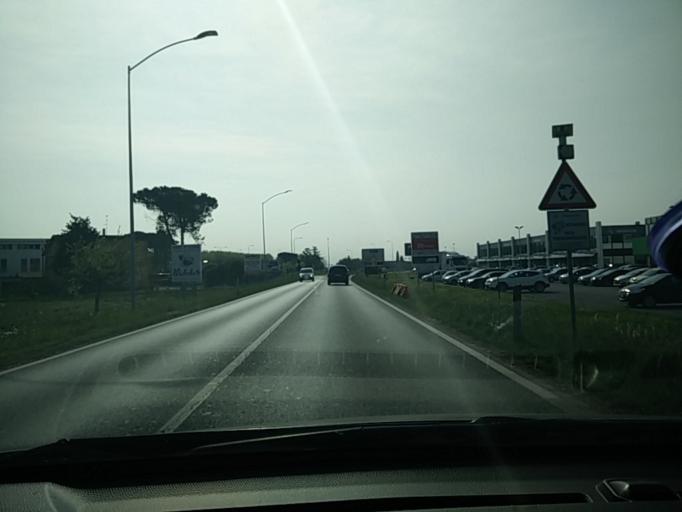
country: IT
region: Friuli Venezia Giulia
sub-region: Provincia di Udine
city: Buttrio
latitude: 46.0107
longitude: 13.3269
